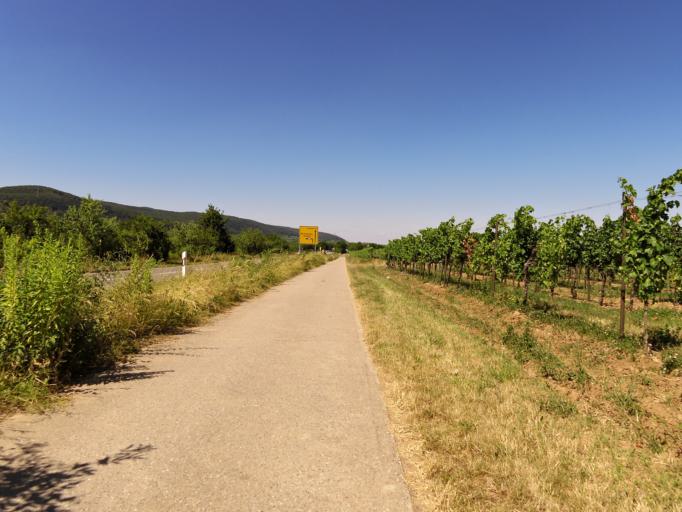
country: DE
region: Rheinland-Pfalz
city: Ruppertsberg
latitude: 49.3793
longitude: 8.1750
